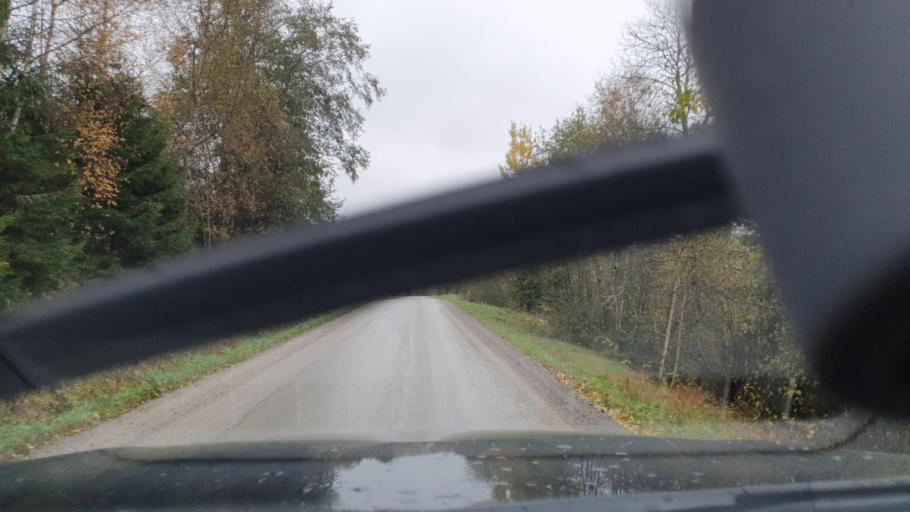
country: SE
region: Vaermland
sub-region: Arvika Kommun
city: Arvika
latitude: 59.8326
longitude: 12.7474
